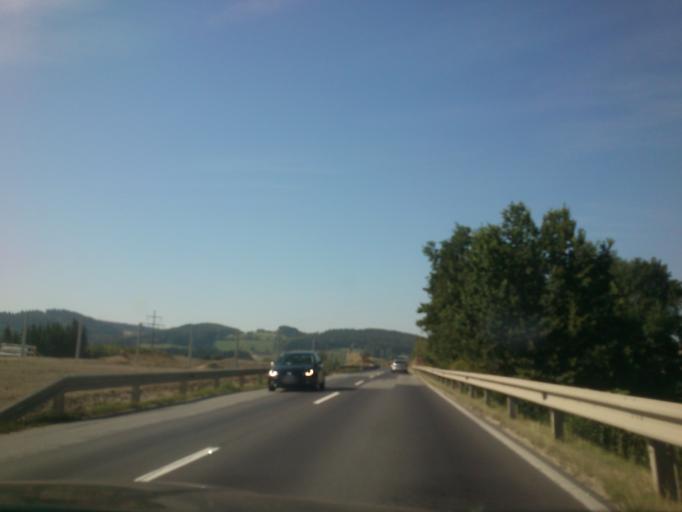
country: AT
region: Upper Austria
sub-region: Politischer Bezirk Freistadt
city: Freistadt
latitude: 48.4525
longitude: 14.4963
